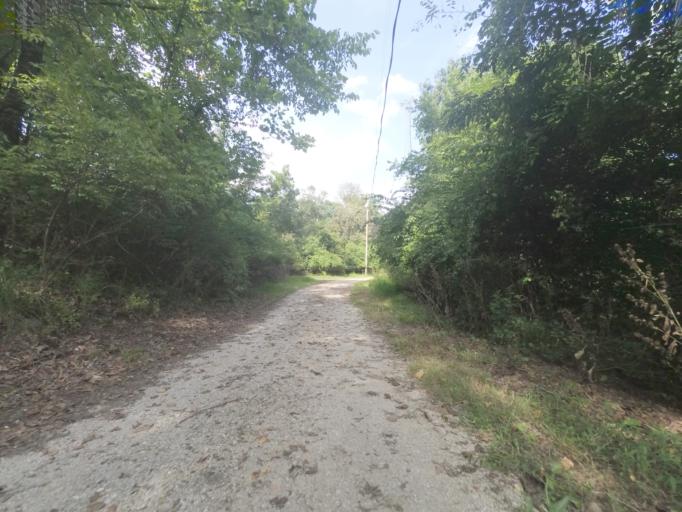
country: US
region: West Virginia
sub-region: Cabell County
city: Huntington
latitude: 38.4194
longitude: -82.4004
